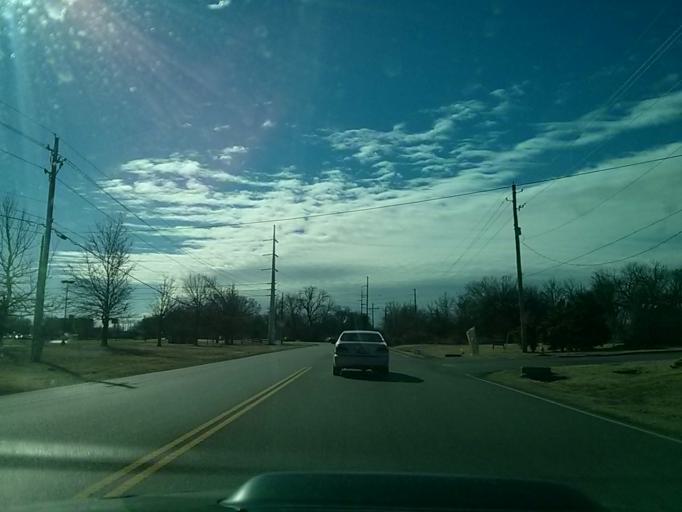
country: US
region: Oklahoma
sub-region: Tulsa County
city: Jenks
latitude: 36.0431
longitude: -95.9578
